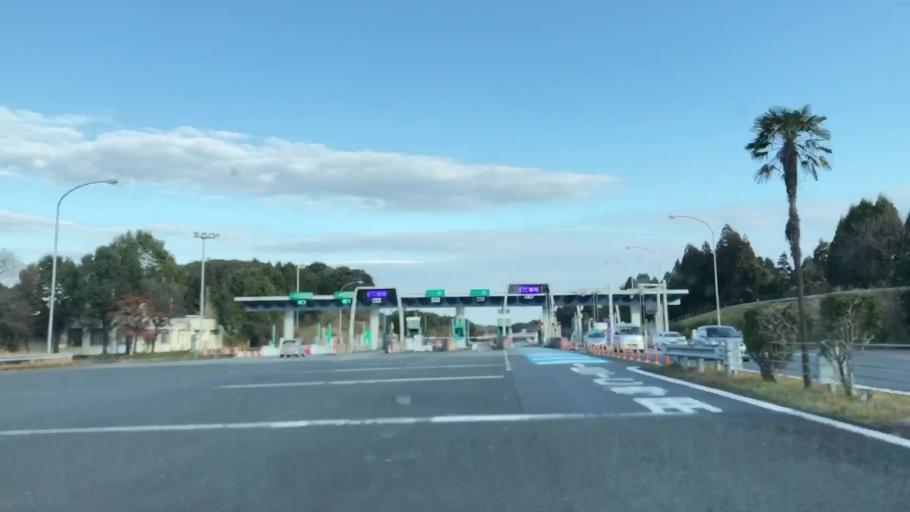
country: JP
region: Miyazaki
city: Miyazaki-shi
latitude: 31.8675
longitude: 131.3973
